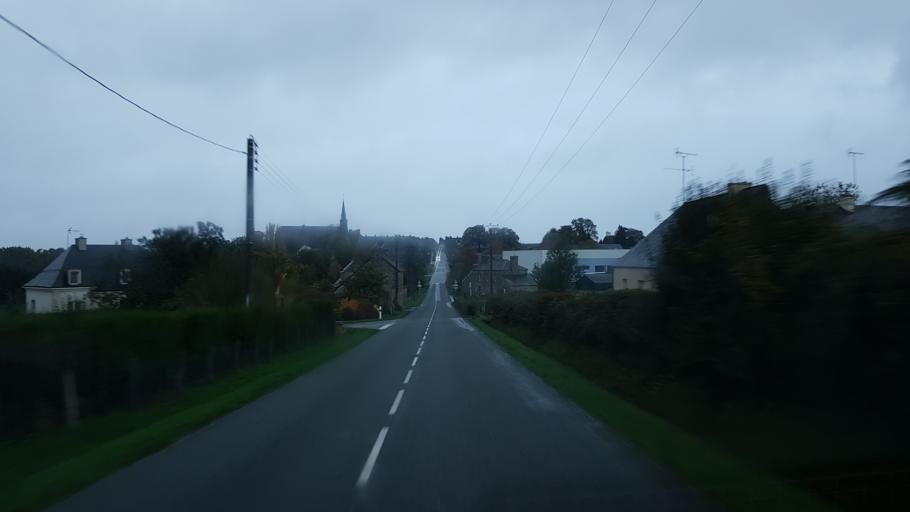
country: FR
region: Pays de la Loire
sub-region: Departement de la Mayenne
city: Juvigne
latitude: 48.2250
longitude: -1.0393
